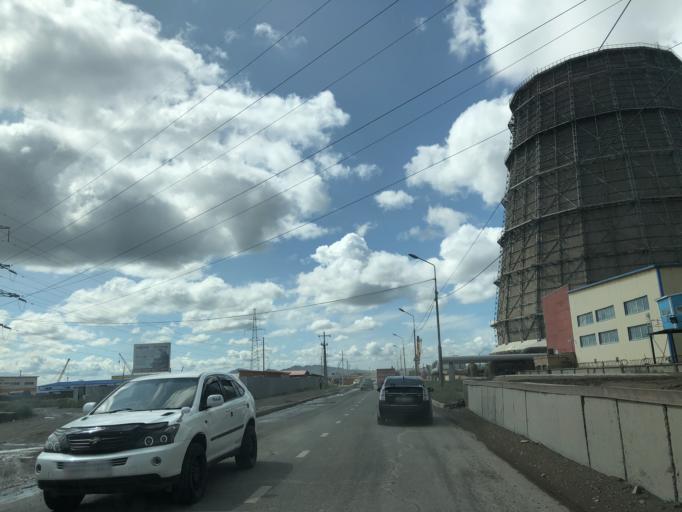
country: MN
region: Ulaanbaatar
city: Ulaanbaatar
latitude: 47.8911
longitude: 106.8024
